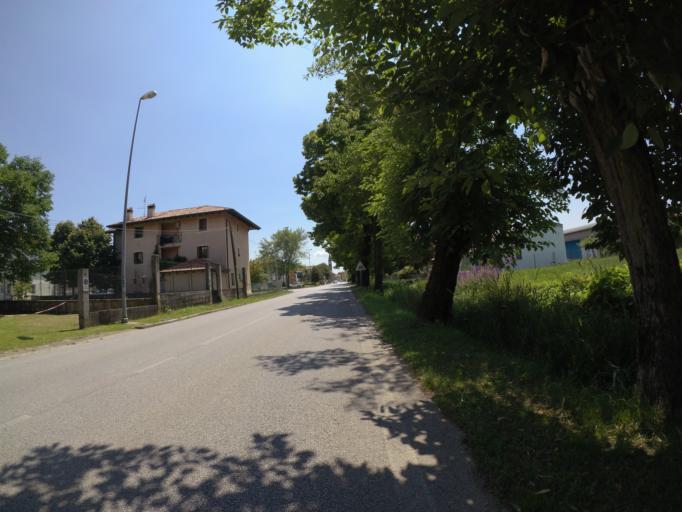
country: IT
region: Friuli Venezia Giulia
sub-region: Provincia di Udine
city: Lestizza
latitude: 45.9587
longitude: 13.1403
